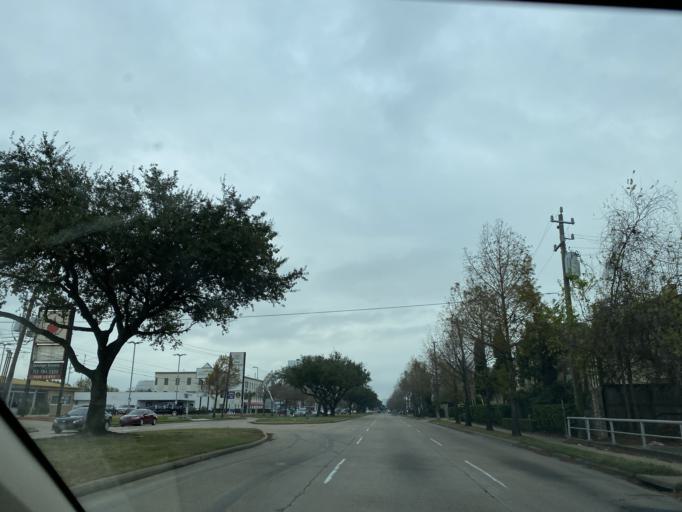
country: US
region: Texas
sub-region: Harris County
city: Piney Point Village
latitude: 29.7317
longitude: -95.4957
